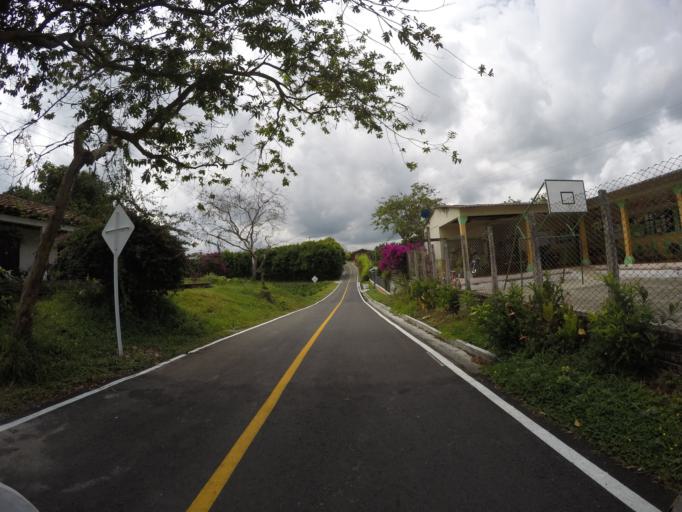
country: CO
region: Quindio
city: Quimbaya
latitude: 4.6140
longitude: -75.7479
